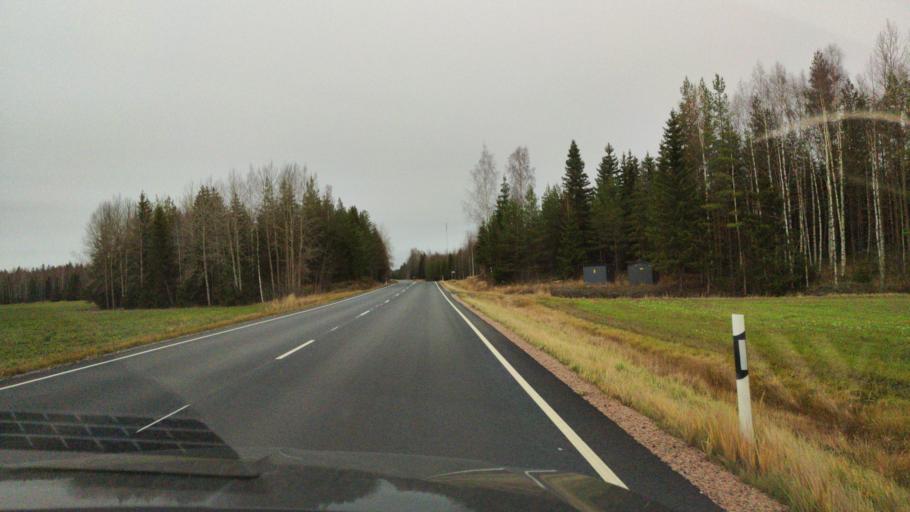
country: FI
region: Varsinais-Suomi
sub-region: Loimaa
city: Aura
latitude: 60.7136
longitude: 22.4441
